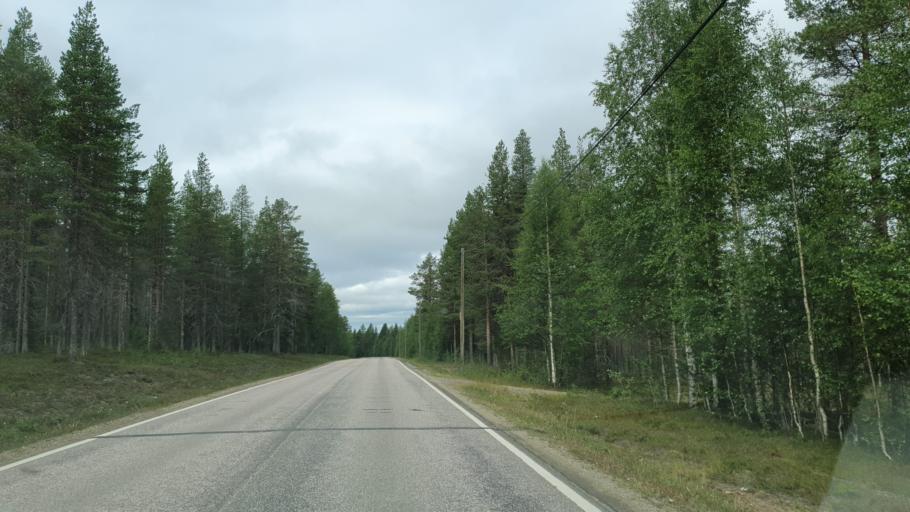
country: FI
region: Lapland
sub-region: Pohjois-Lappi
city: Sodankylae
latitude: 67.4165
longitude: 26.2859
